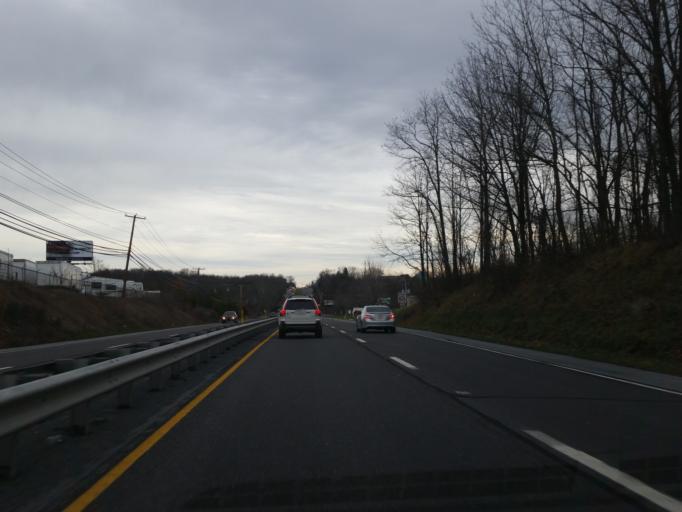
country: US
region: Pennsylvania
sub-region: Dauphin County
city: Linglestown
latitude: 40.3277
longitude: -76.7658
